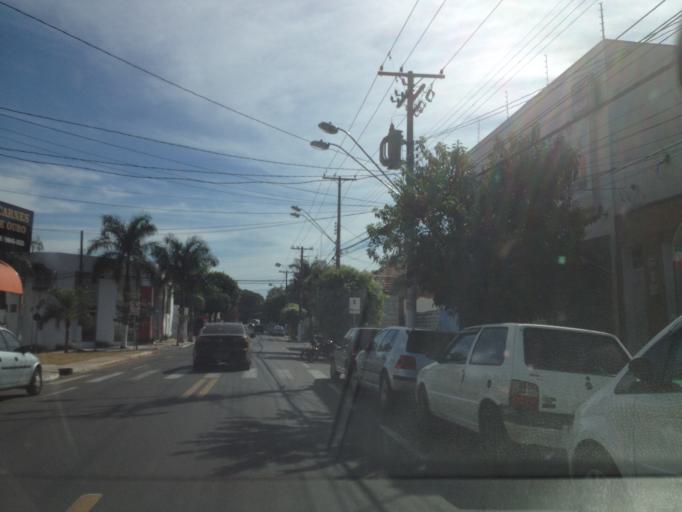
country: BR
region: Sao Paulo
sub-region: Marilia
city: Marilia
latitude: -22.2151
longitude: -49.9395
